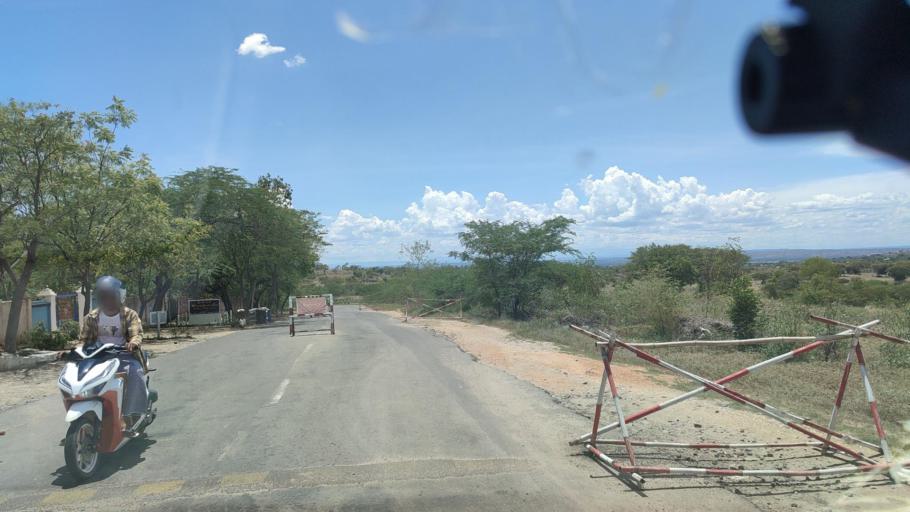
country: MM
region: Magway
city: Chauk
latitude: 20.8444
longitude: 94.8457
